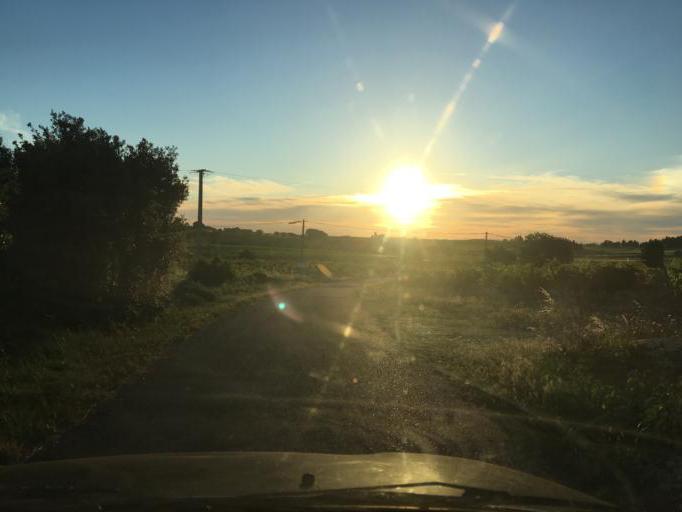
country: FR
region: Provence-Alpes-Cote d'Azur
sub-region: Departement du Vaucluse
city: Chateauneuf-du-Pape
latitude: 44.0740
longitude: 4.8337
